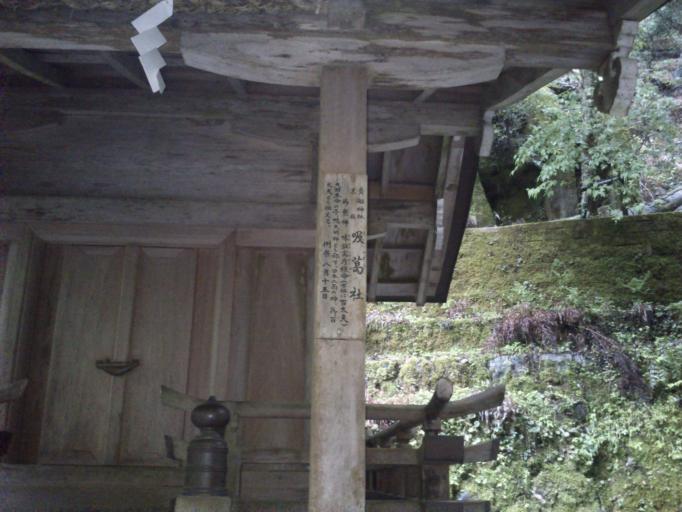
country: JP
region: Kyoto
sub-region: Kyoto-shi
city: Kamigyo-ku
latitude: 35.1289
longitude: 135.7652
